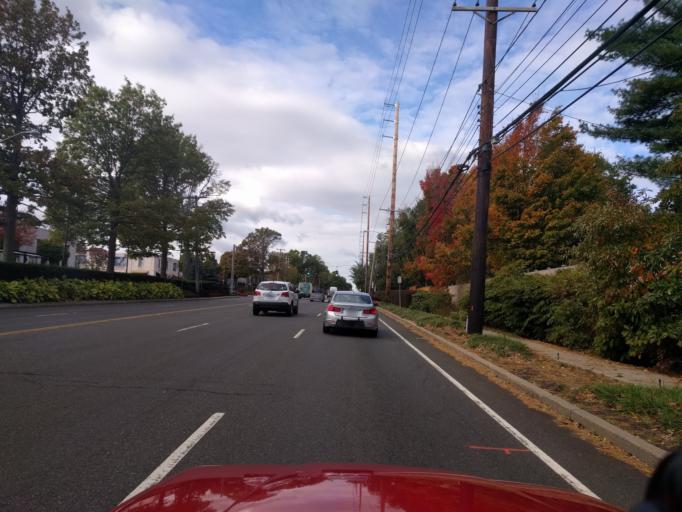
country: US
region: New York
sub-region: Nassau County
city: Munsey Park
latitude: 40.7965
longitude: -73.6721
